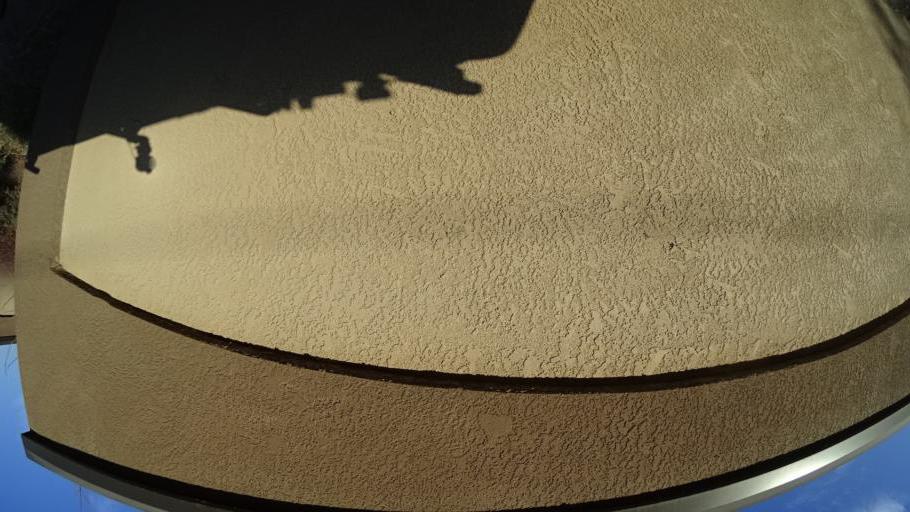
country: US
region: California
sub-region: Kern County
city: Greenacres
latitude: 35.4296
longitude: -119.1235
